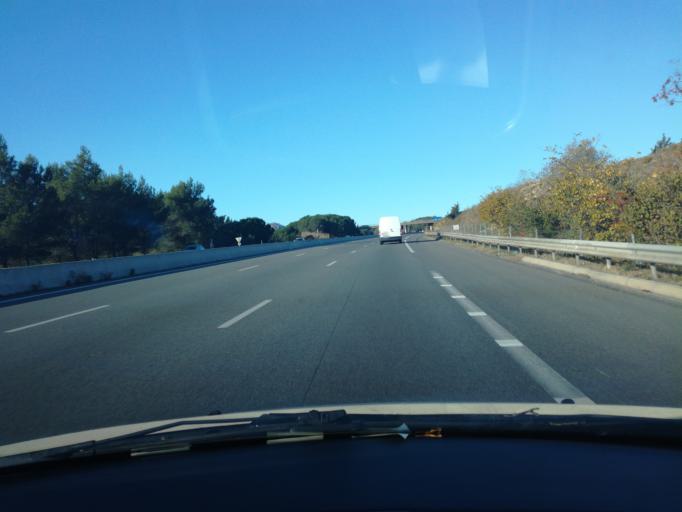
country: FR
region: Provence-Alpes-Cote d'Azur
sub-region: Departement du Var
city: Puget-sur-Argens
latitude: 43.4575
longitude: 6.6970
